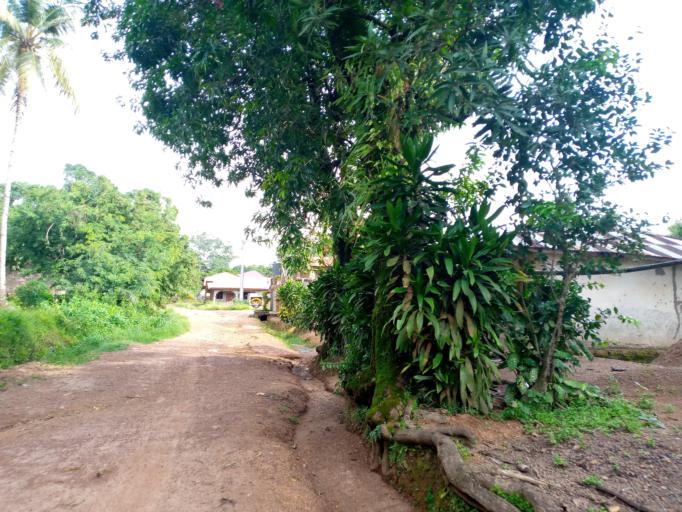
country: SL
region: Northern Province
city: Magburaka
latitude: 8.7180
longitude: -11.9509
